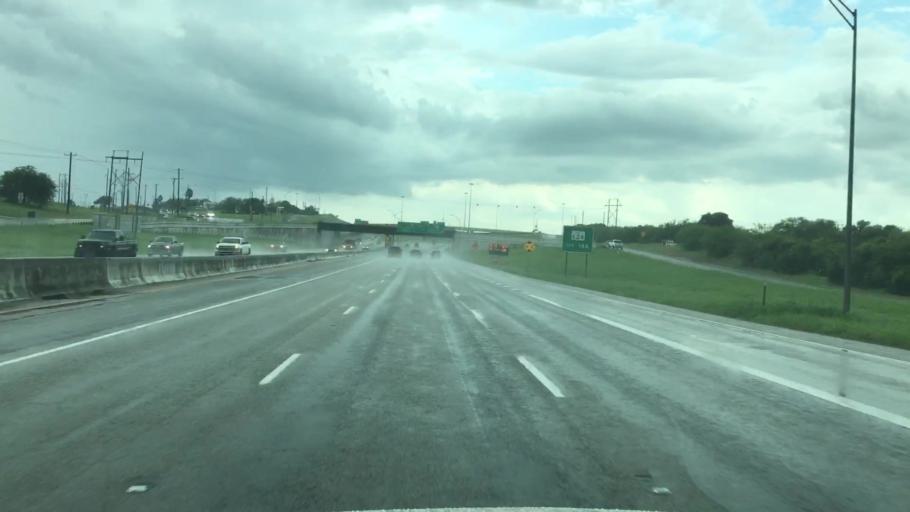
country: US
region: Texas
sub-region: Nueces County
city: Robstown
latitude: 27.8611
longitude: -97.6136
